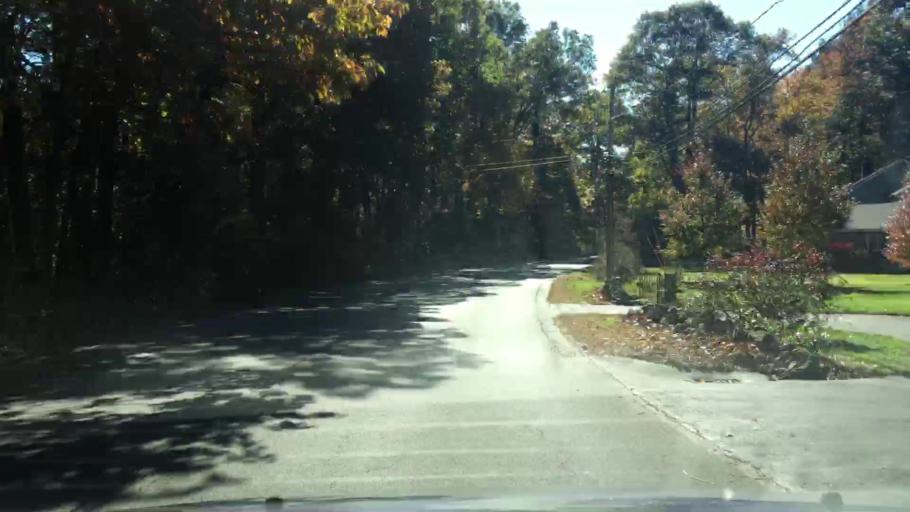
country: US
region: Massachusetts
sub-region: Essex County
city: North Andover
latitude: 42.6906
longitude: -71.0709
